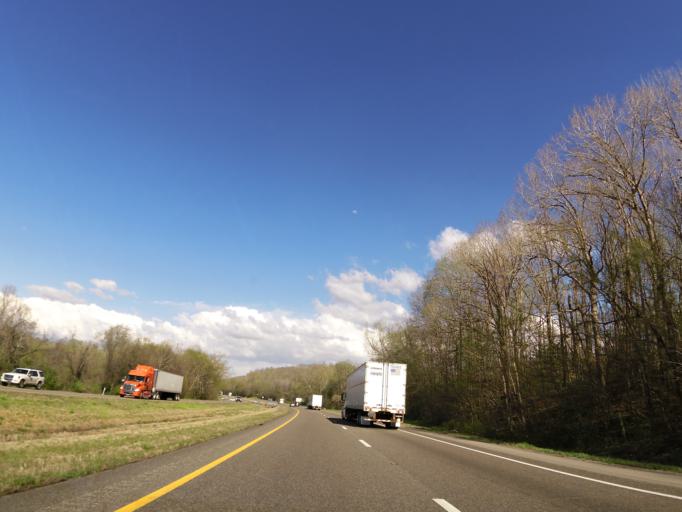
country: US
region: Tennessee
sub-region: Humphreys County
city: New Johnsonville
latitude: 35.8646
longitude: -87.8932
